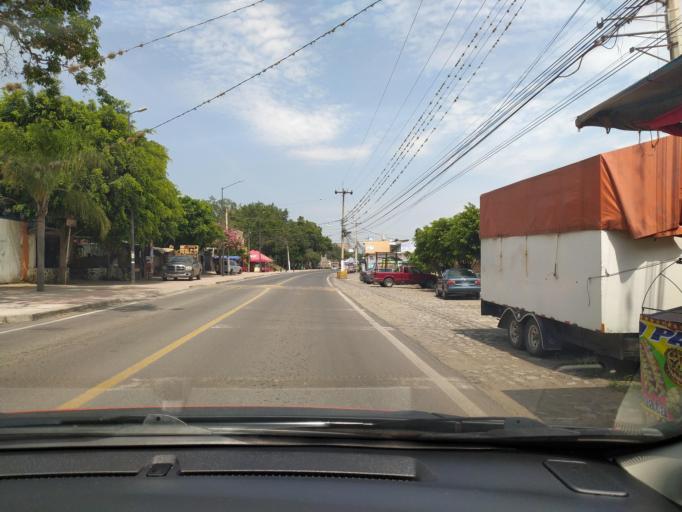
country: MX
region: Jalisco
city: San Juan Cosala
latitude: 20.2881
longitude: -103.3403
